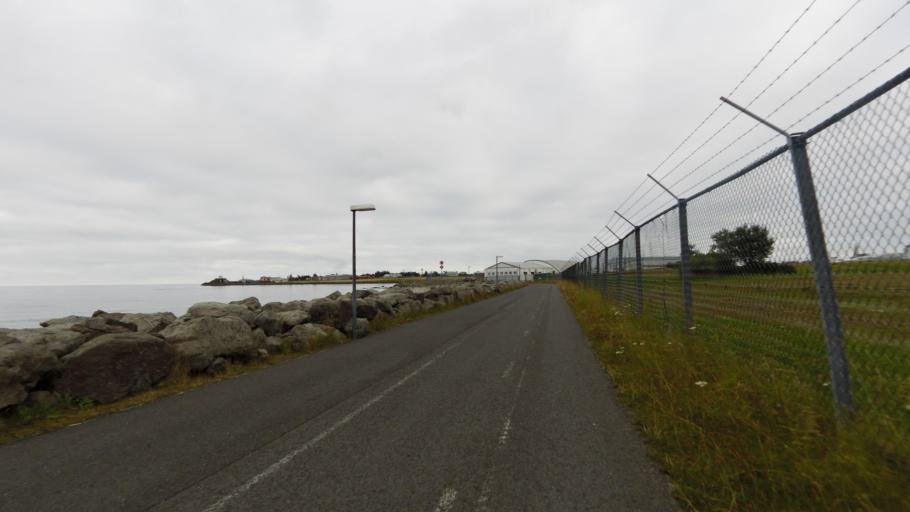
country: IS
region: Capital Region
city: Kopavogur
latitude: 64.1218
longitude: -21.9391
